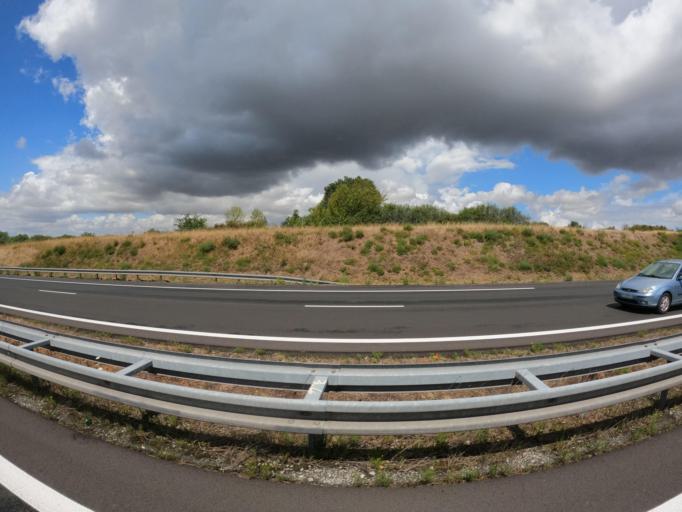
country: FR
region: Pays de la Loire
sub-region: Departement de Maine-et-Loire
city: Saint-Leger-des-Bois
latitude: 47.4589
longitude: -0.7000
